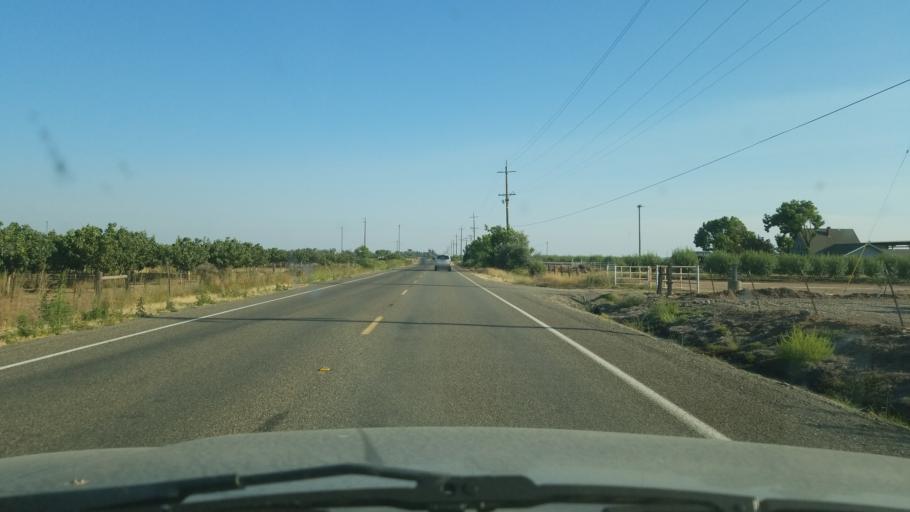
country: US
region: California
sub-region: Merced County
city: Merced
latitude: 37.3870
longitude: -120.4682
